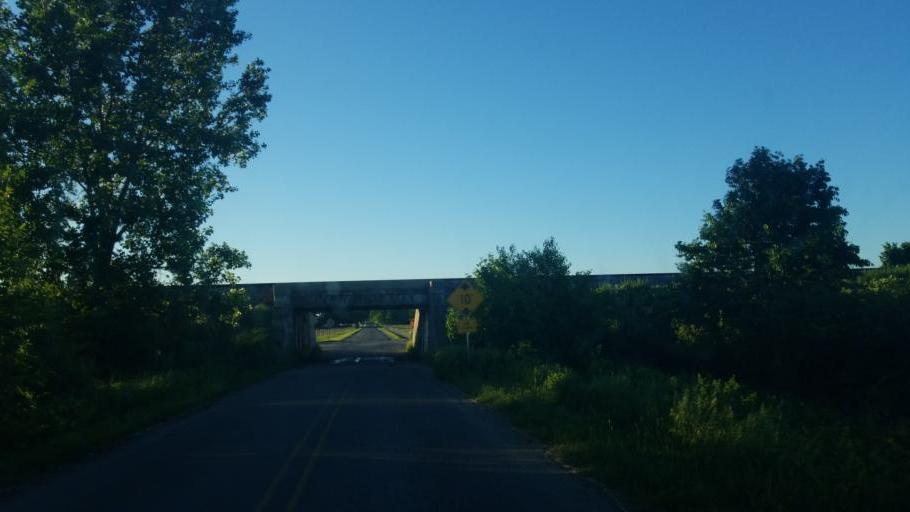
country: US
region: Indiana
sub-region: Elkhart County
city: Nappanee
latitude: 41.4440
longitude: -86.0496
